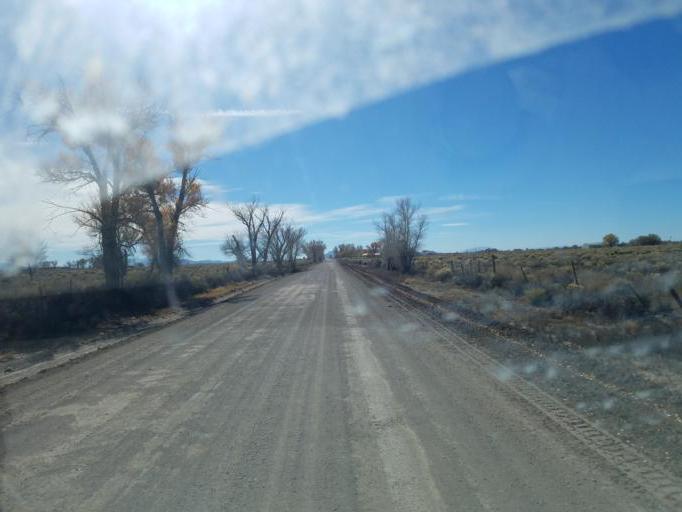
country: US
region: Colorado
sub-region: Alamosa County
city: Alamosa East
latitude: 37.4926
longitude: -105.7849
